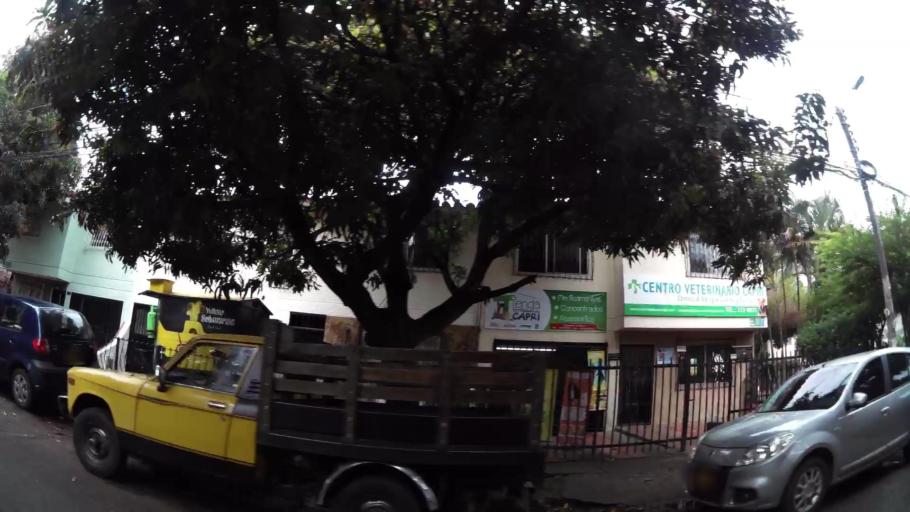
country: CO
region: Valle del Cauca
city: Cali
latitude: 3.3913
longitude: -76.5401
